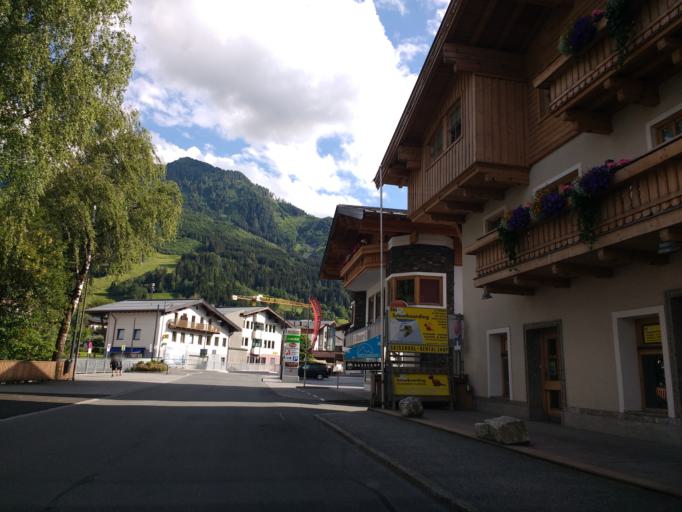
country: AT
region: Salzburg
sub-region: Politischer Bezirk Zell am See
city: Kaprun
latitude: 47.2736
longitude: 12.7588
